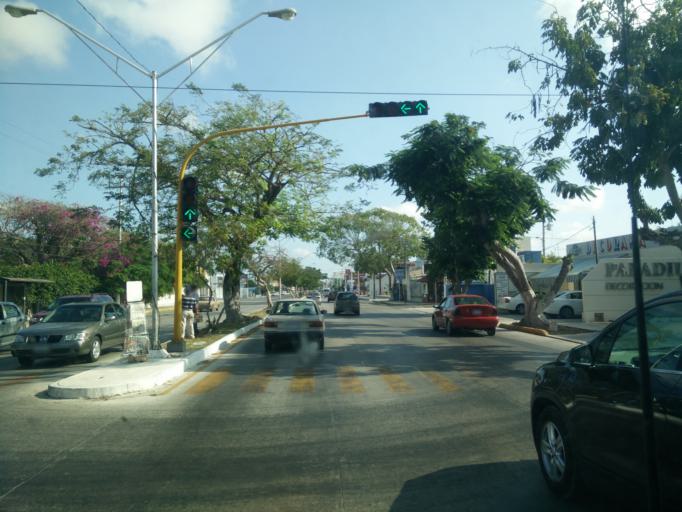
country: MX
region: Yucatan
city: Merida
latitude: 21.0063
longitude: -89.6144
